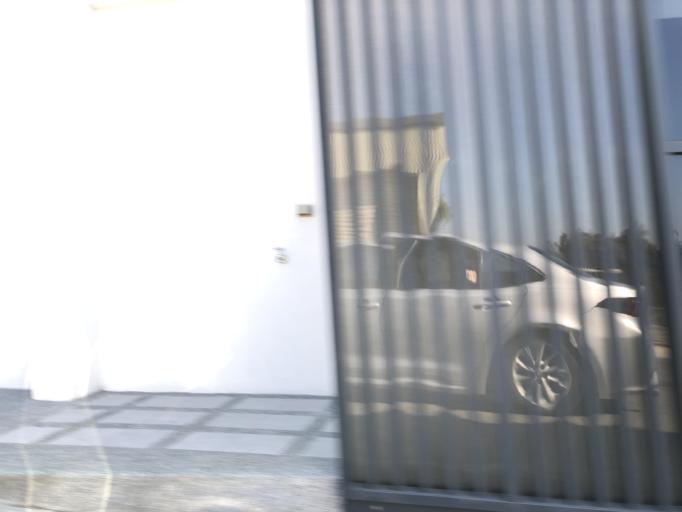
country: TW
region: Taiwan
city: Yujing
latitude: 23.0395
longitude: 120.3600
